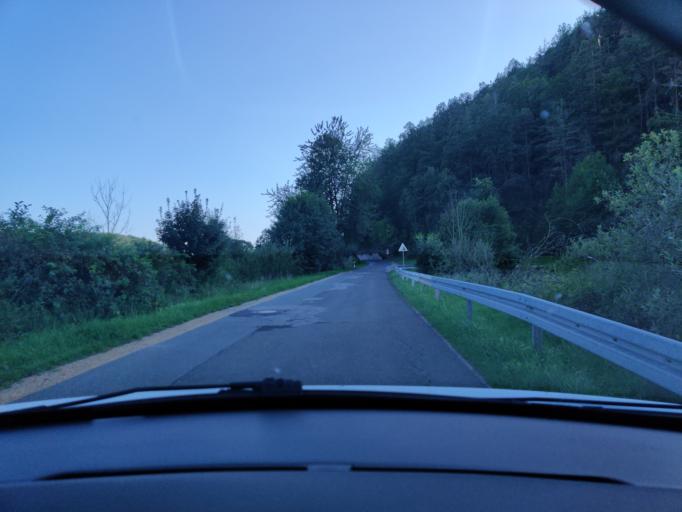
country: DE
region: Bavaria
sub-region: Upper Palatinate
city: Nabburg
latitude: 49.4324
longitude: 12.1689
